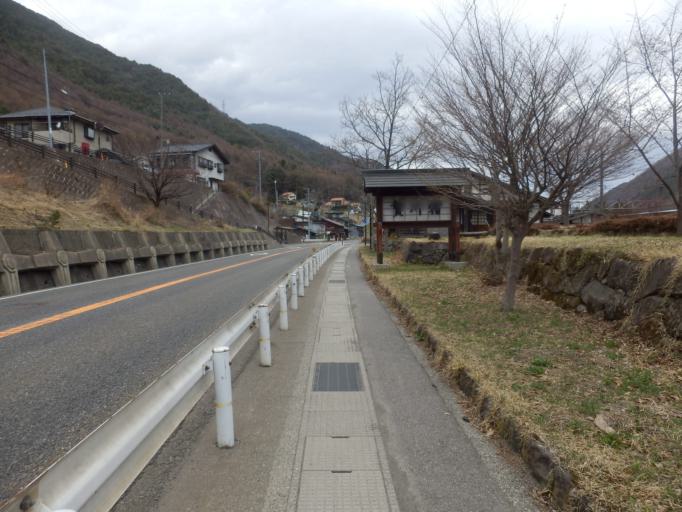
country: JP
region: Nagano
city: Shiojiri
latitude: 36.0131
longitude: 137.8601
